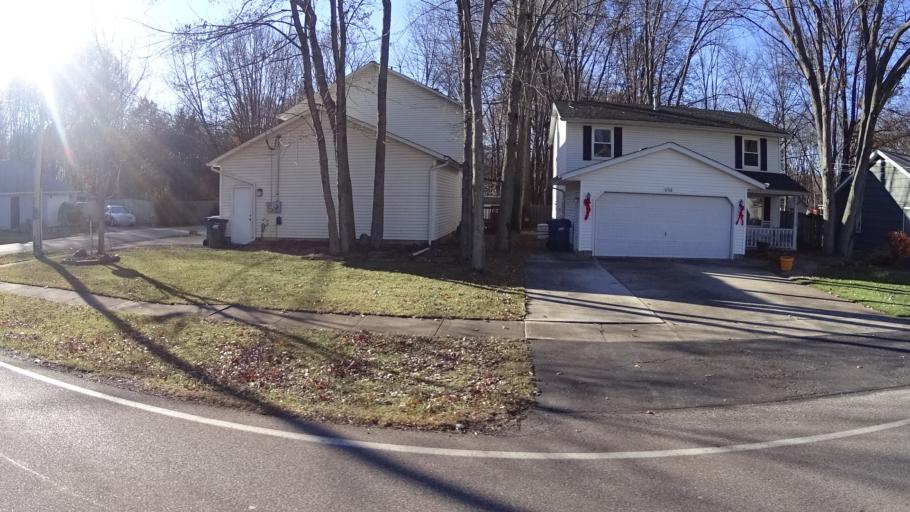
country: US
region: Ohio
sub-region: Lorain County
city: North Ridgeville
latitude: 41.3944
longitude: -82.0111
